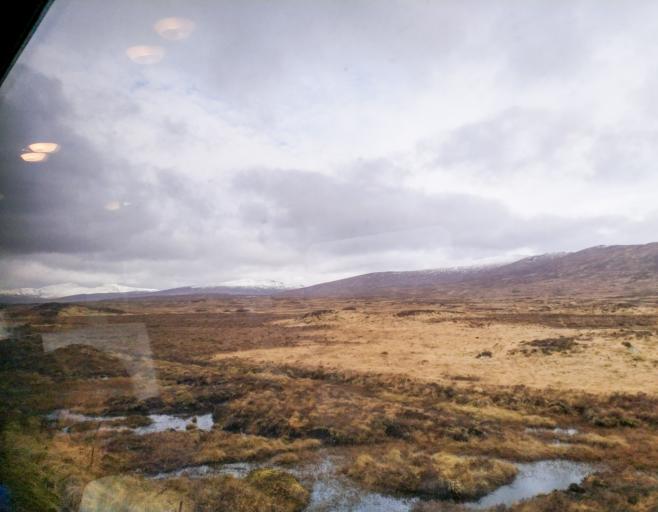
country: GB
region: Scotland
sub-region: Highland
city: Spean Bridge
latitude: 56.7059
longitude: -4.5932
